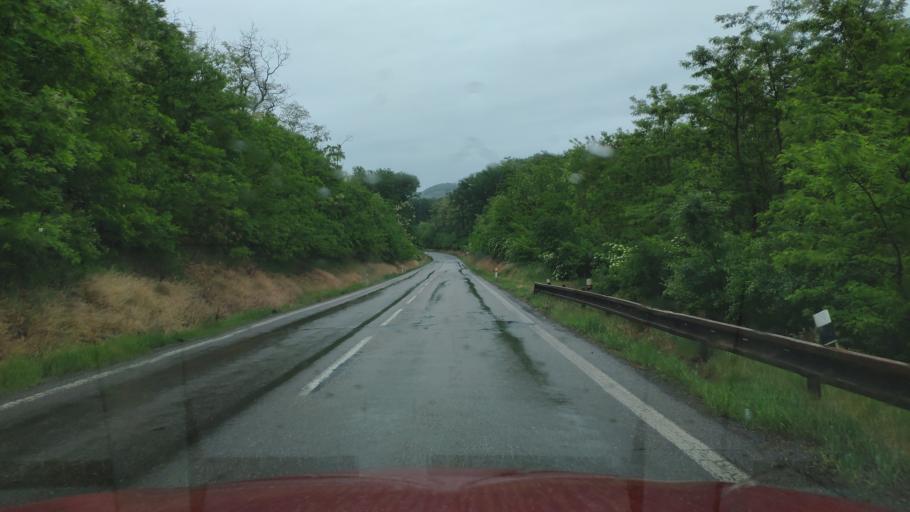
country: HU
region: Borsod-Abauj-Zemplen
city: Ricse
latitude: 48.4402
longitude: 21.9448
